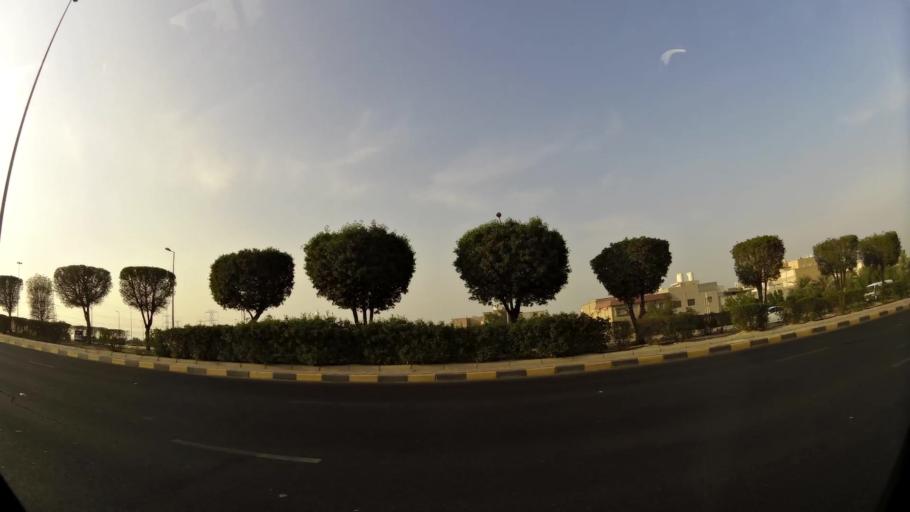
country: KW
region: Mubarak al Kabir
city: Sabah as Salim
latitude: 29.2394
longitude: 48.0523
